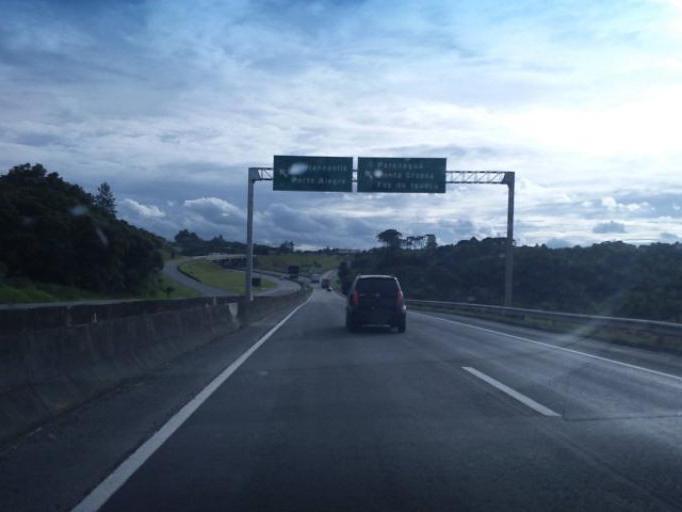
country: BR
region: Parana
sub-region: Campina Grande Do Sul
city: Campina Grande do Sul
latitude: -25.3420
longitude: -49.0413
